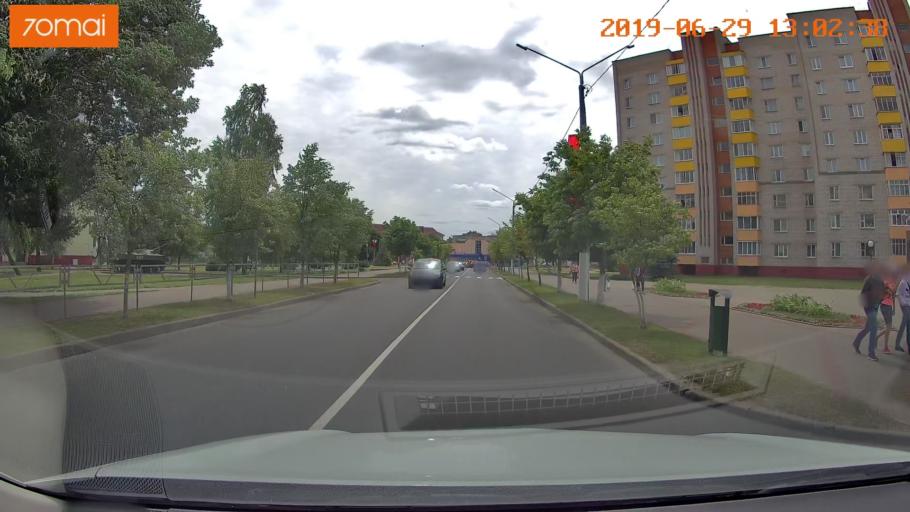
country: BY
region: Minsk
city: Slutsk
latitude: 53.0346
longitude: 27.5599
